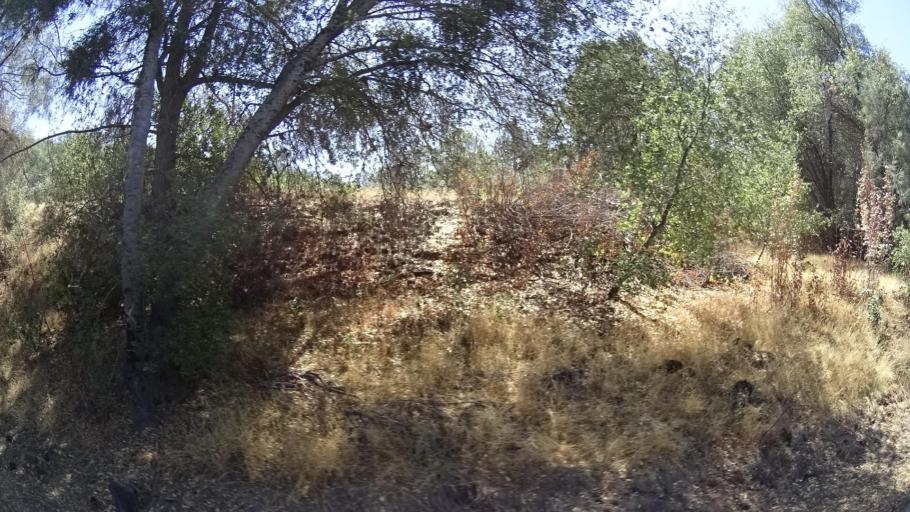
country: US
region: California
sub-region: Mariposa County
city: Mariposa
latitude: 37.4227
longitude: -119.9067
